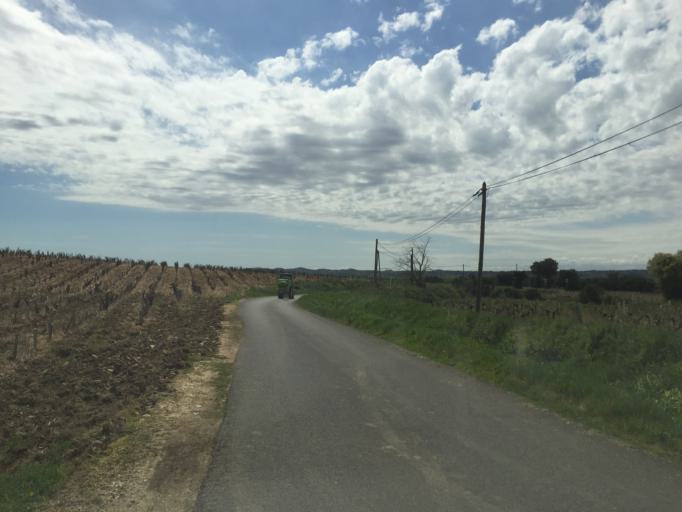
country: FR
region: Provence-Alpes-Cote d'Azur
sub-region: Departement du Vaucluse
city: Chateauneuf-du-Pape
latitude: 44.0568
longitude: 4.8161
